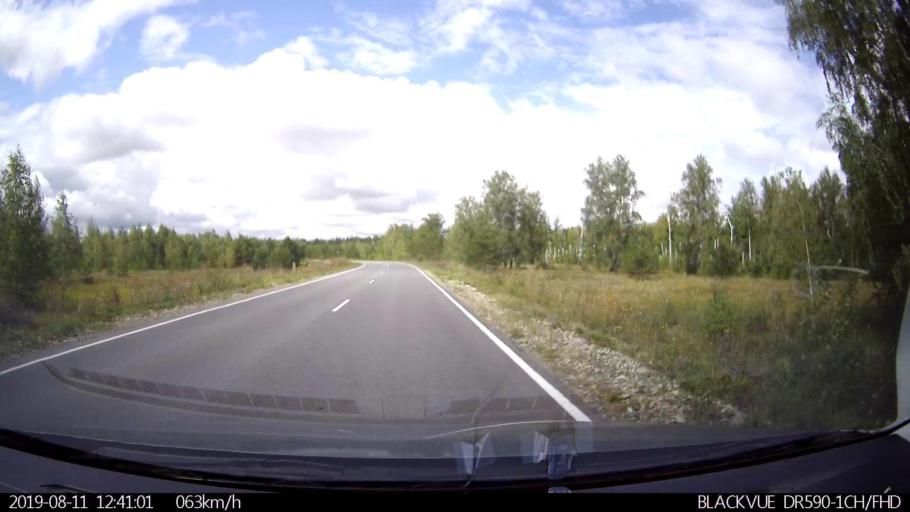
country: RU
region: Ulyanovsk
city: Ignatovka
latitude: 53.8419
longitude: 47.7725
